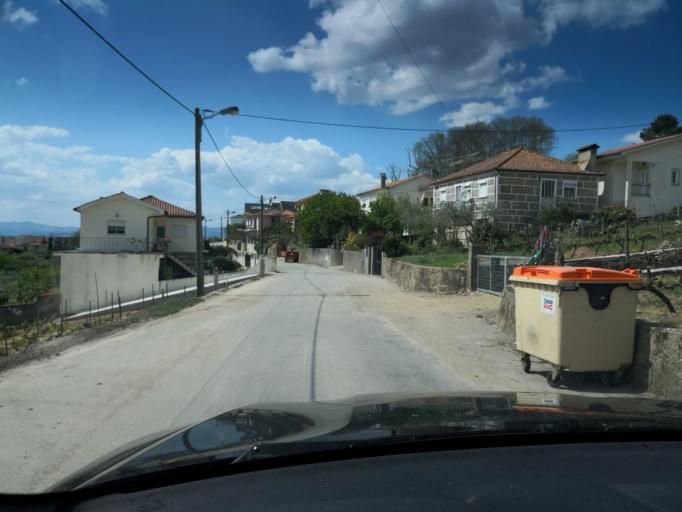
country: PT
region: Vila Real
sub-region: Vila Real
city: Vila Real
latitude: 41.2266
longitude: -7.6951
